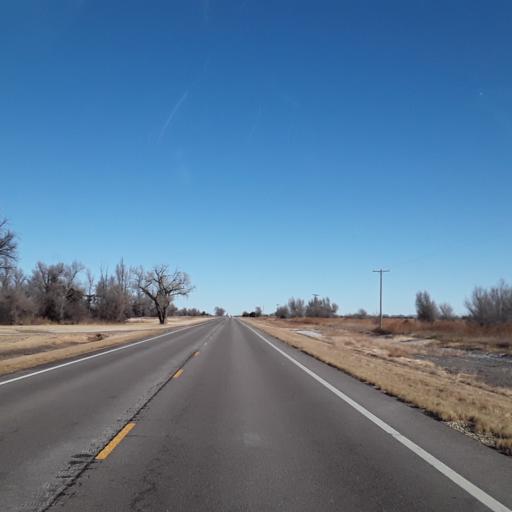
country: US
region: Kansas
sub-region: Pawnee County
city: Larned
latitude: 38.1170
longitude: -99.1836
